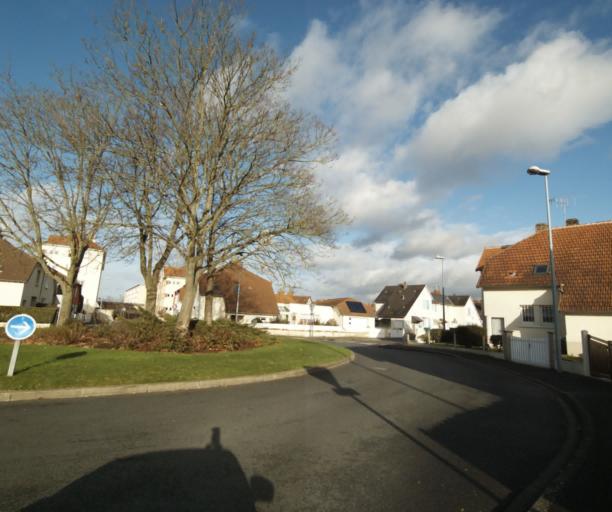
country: FR
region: Pays de la Loire
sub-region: Departement de la Sarthe
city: Le Mans
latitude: 47.9671
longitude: 0.2078
